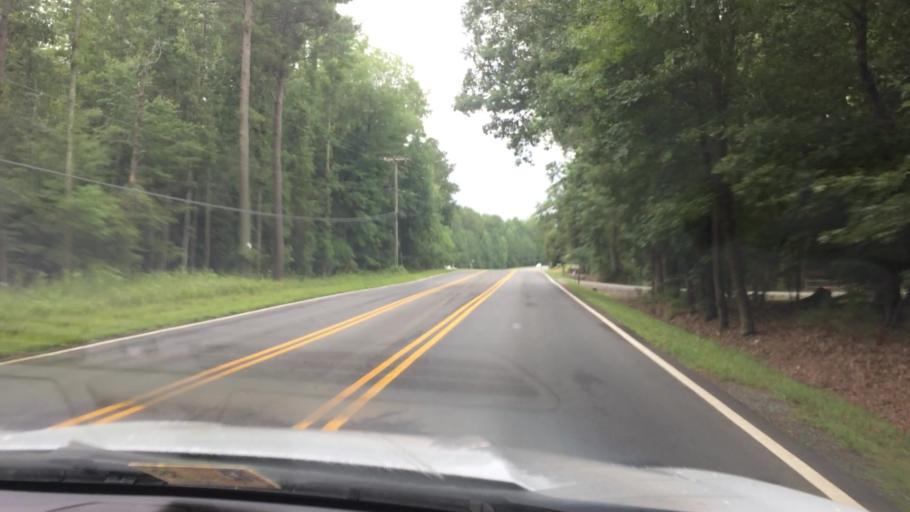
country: US
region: Virginia
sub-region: New Kent County
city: New Kent
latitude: 37.4674
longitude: -77.0336
